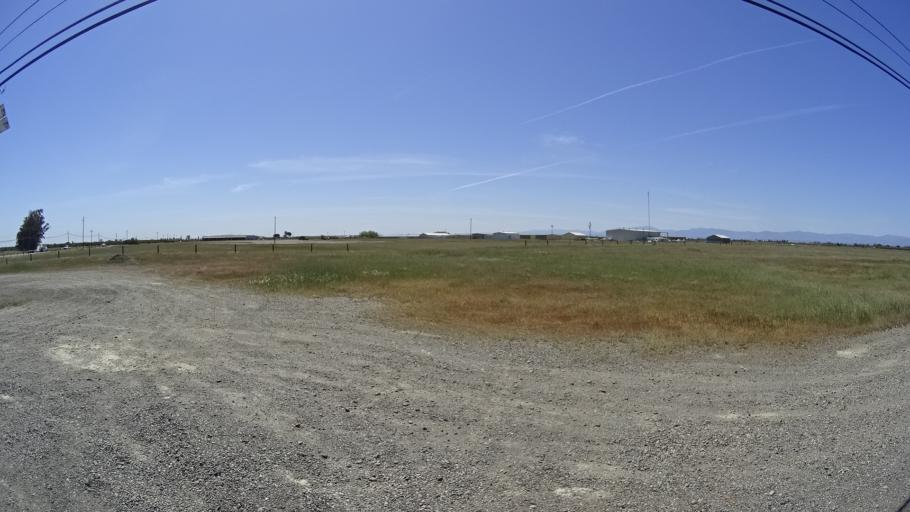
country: US
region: California
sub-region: Glenn County
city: Orland
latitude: 39.7255
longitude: -122.1420
